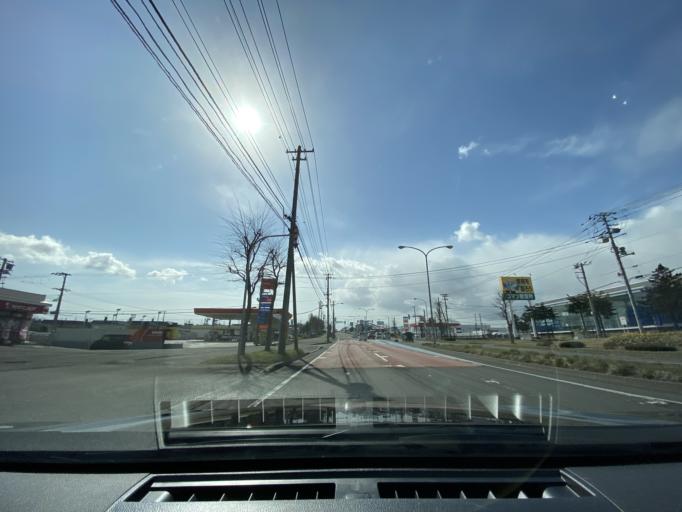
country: JP
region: Hokkaido
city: Kitahiroshima
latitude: 42.9662
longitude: 141.4852
